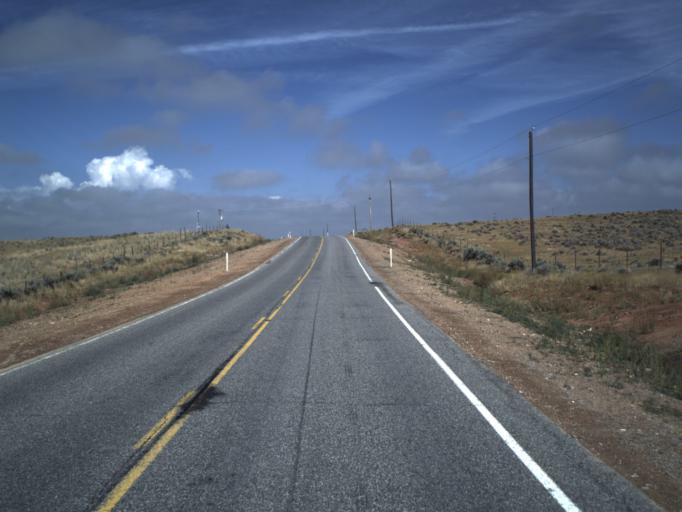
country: US
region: Wyoming
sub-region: Uinta County
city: Evanston
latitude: 41.4194
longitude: -111.0495
